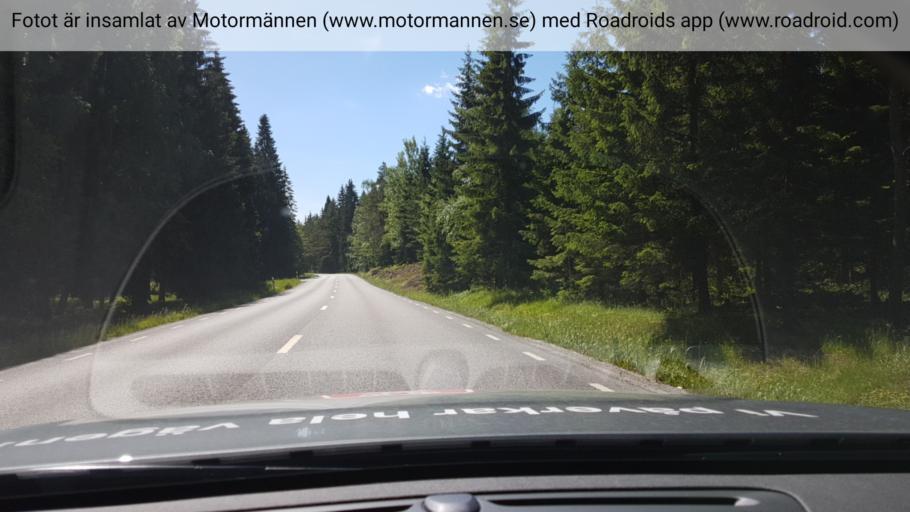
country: SE
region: Stockholm
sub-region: Haninge Kommun
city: Haninge
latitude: 59.1517
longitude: 18.1795
